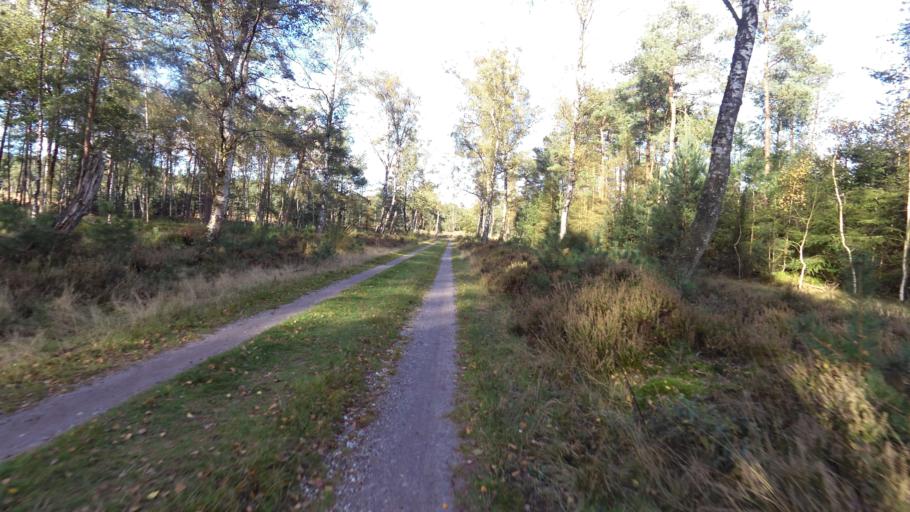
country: NL
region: Gelderland
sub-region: Gemeente Epe
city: Epe
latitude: 52.3869
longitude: 5.9594
